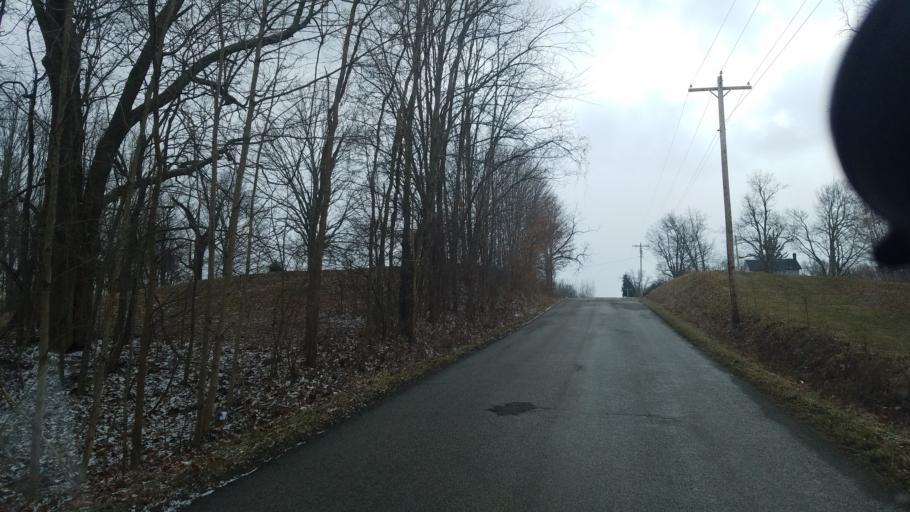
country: US
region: Ohio
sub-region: Morrow County
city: Mount Gilead
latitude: 40.5790
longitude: -82.8053
